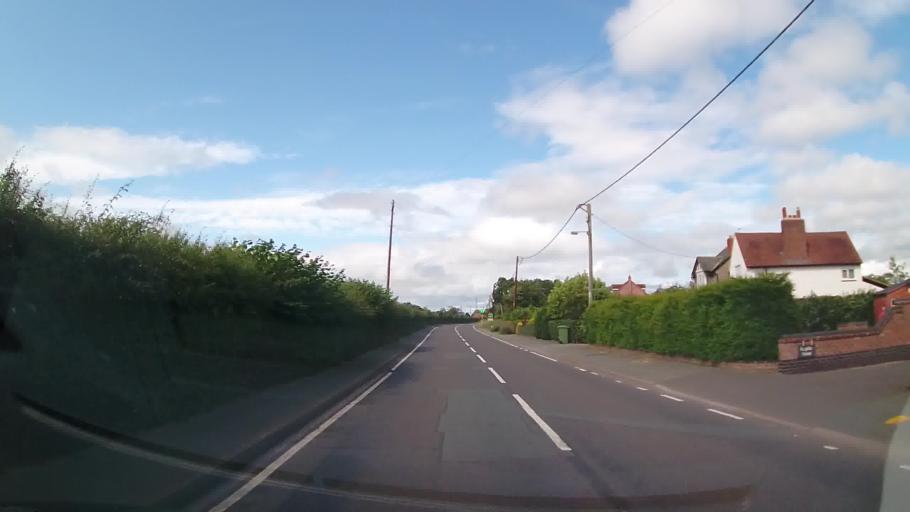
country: GB
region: England
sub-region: Shropshire
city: Petton
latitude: 52.7957
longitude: -2.8517
